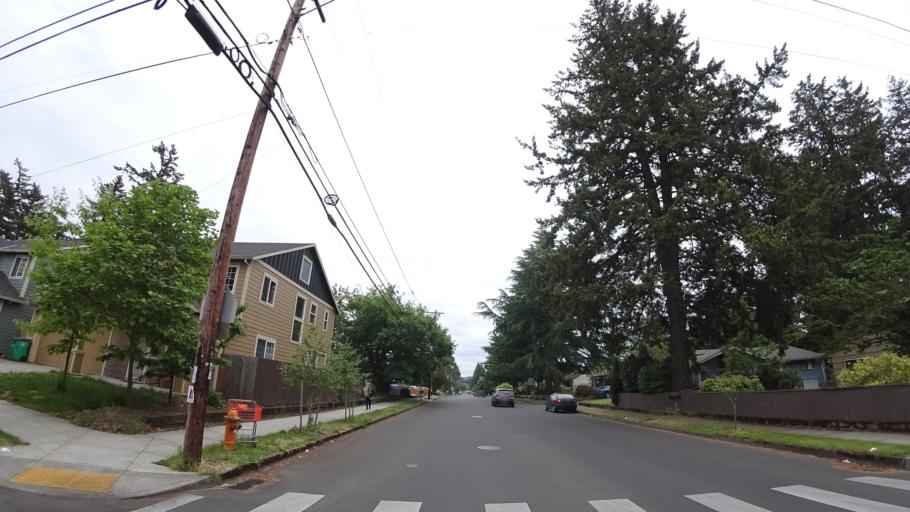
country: US
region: Oregon
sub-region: Multnomah County
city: Lents
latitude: 45.5080
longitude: -122.5299
